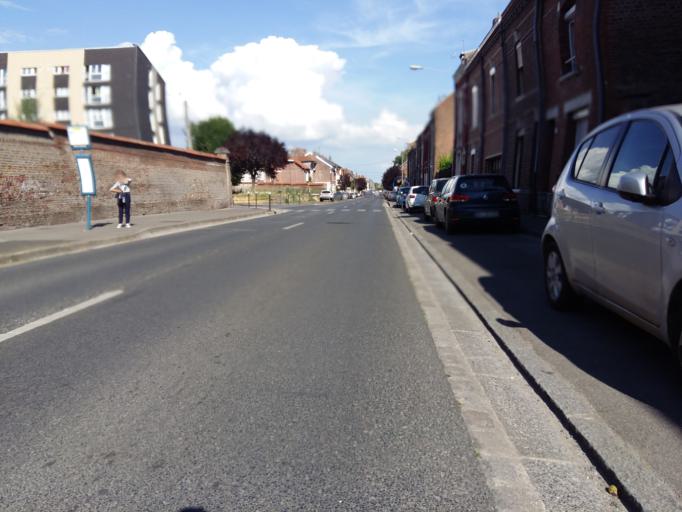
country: FR
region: Picardie
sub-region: Departement de la Somme
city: Rivery
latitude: 49.9029
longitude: 2.3180
